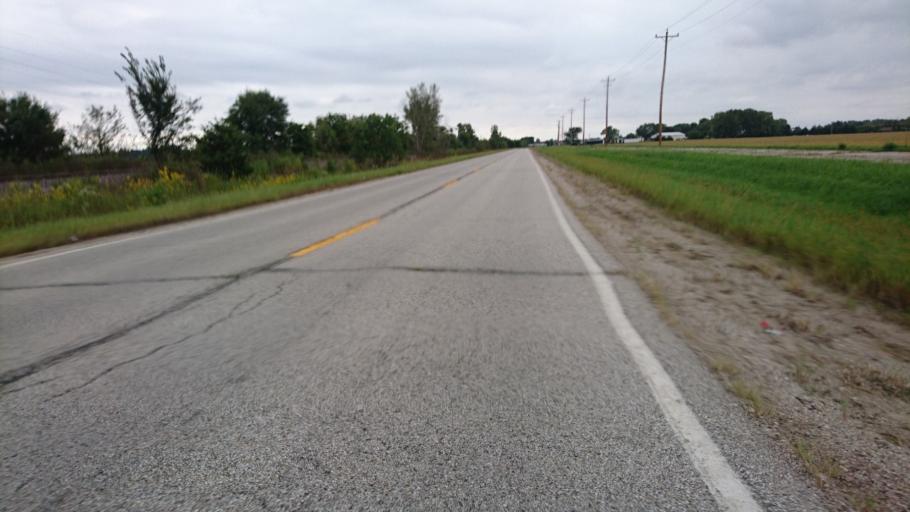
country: US
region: Illinois
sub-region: Livingston County
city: Pontiac
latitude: 40.9047
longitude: -88.6173
